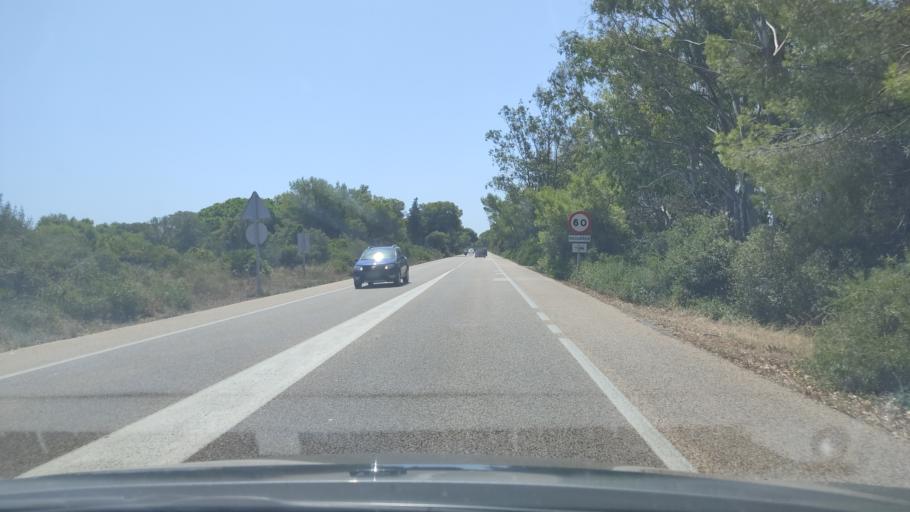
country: ES
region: Valencia
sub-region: Provincia de Valencia
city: Sollana
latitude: 39.3190
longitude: -0.3068
